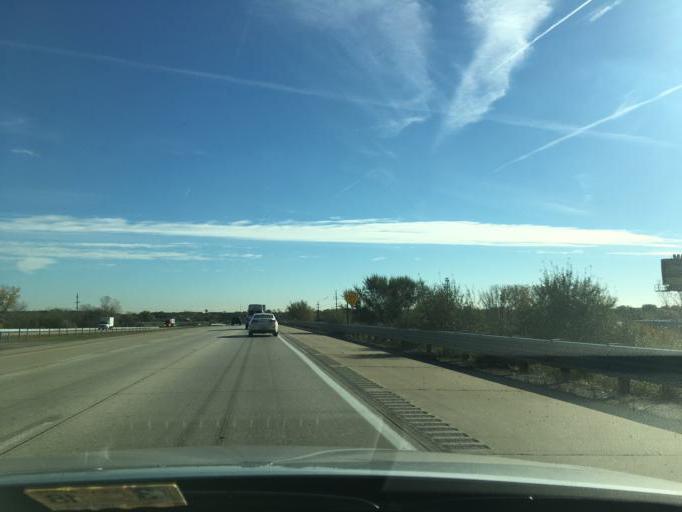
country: US
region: Michigan
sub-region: Wayne County
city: Plymouth
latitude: 42.3830
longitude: -83.4851
